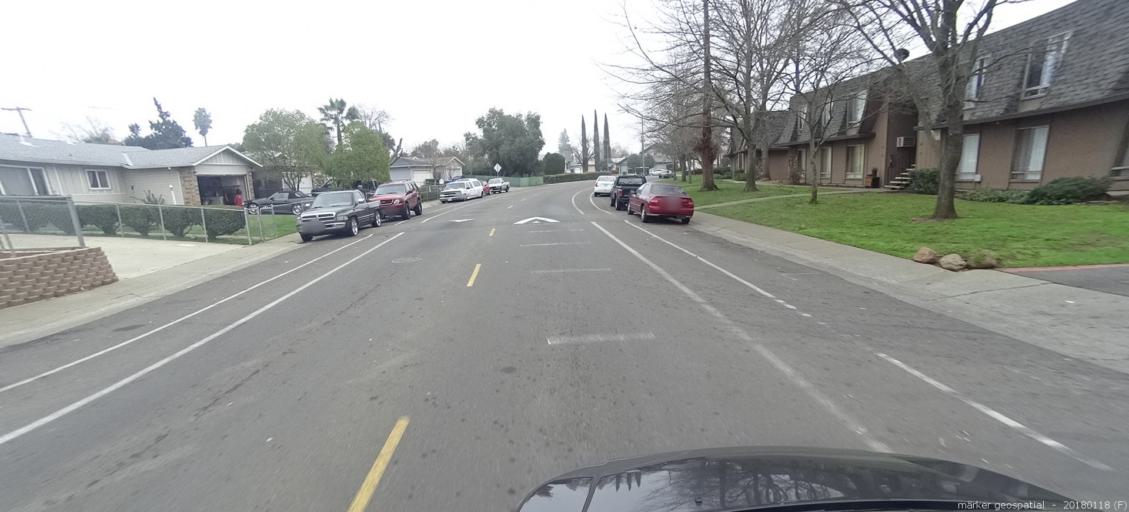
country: US
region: California
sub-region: Sacramento County
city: Rancho Cordova
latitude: 38.5763
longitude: -121.3039
